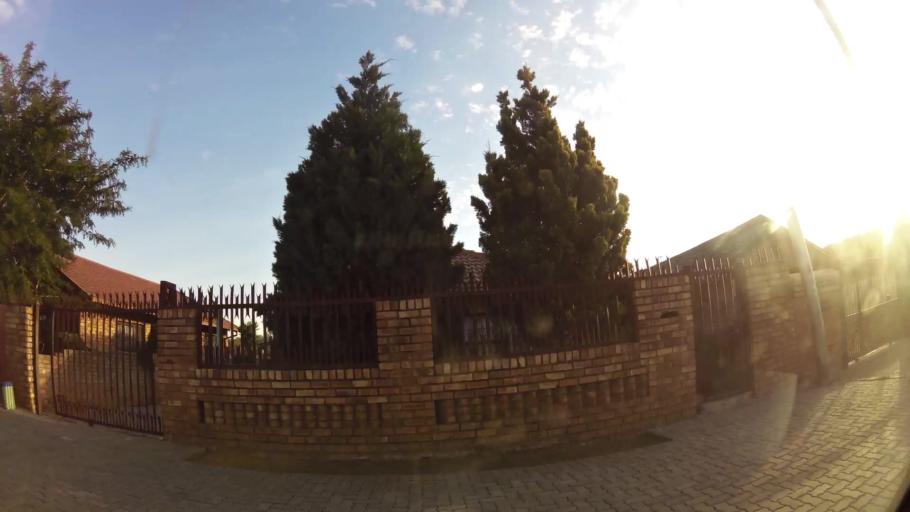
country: ZA
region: Gauteng
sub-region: City of Tshwane Metropolitan Municipality
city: Cullinan
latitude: -25.7146
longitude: 28.3705
